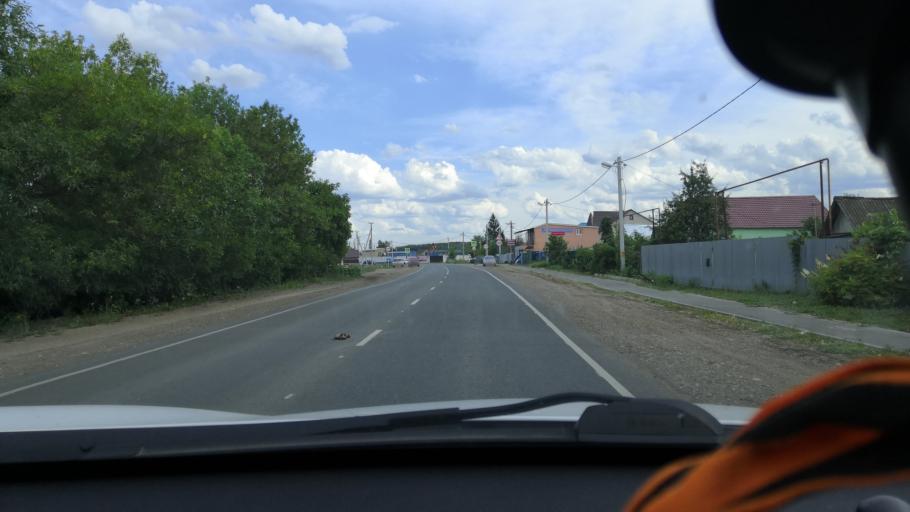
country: RU
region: Samara
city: Novosemeykino
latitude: 53.3802
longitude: 50.3357
